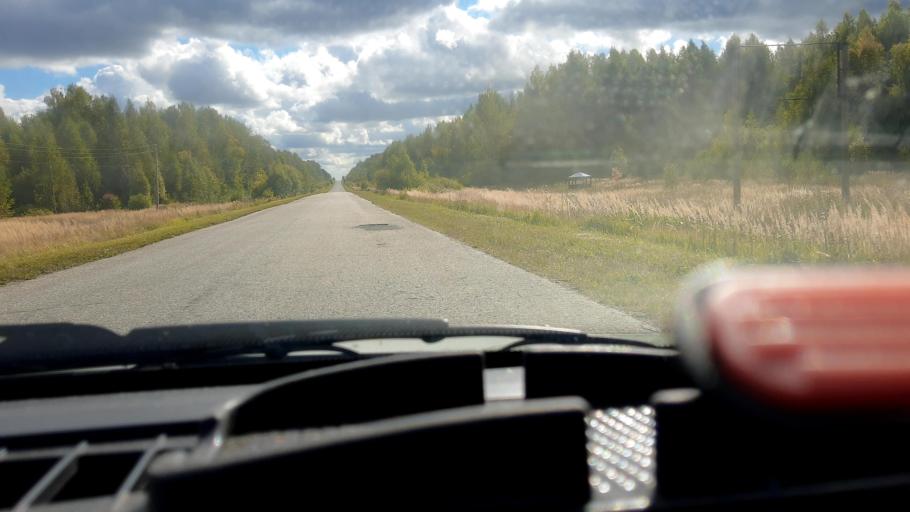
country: RU
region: Mariy-El
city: Kilemary
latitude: 56.9311
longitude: 46.7015
